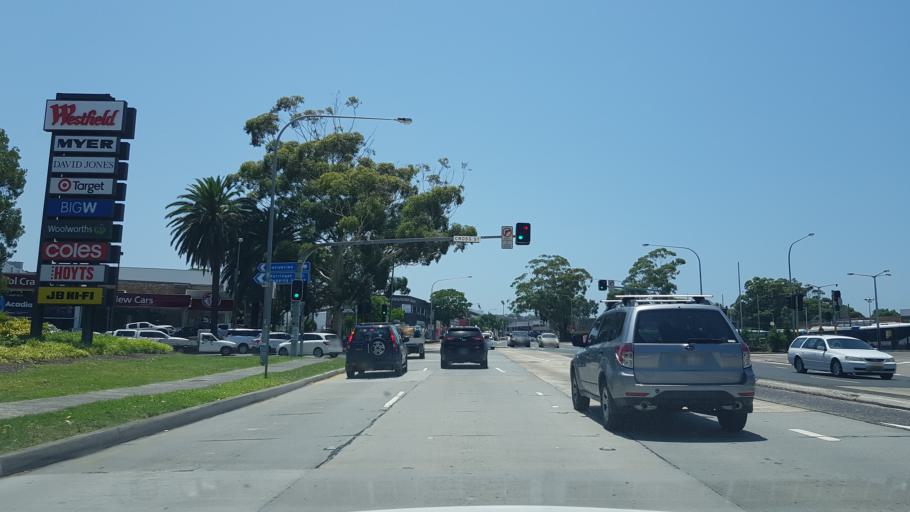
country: AU
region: New South Wales
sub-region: Warringah
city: Brookvale
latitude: -33.7665
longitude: 151.2692
